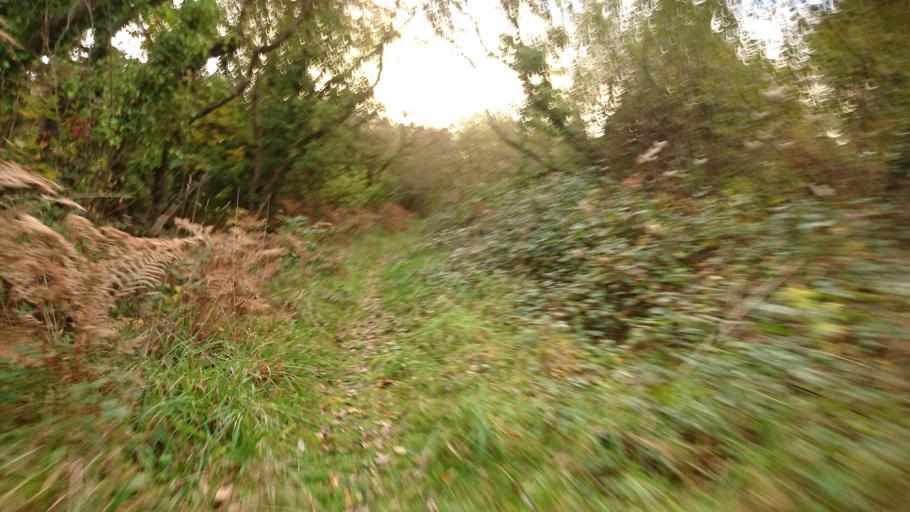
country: FR
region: Brittany
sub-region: Departement du Finistere
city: Lampaul-Plouarzel
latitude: 48.4377
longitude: -4.7700
